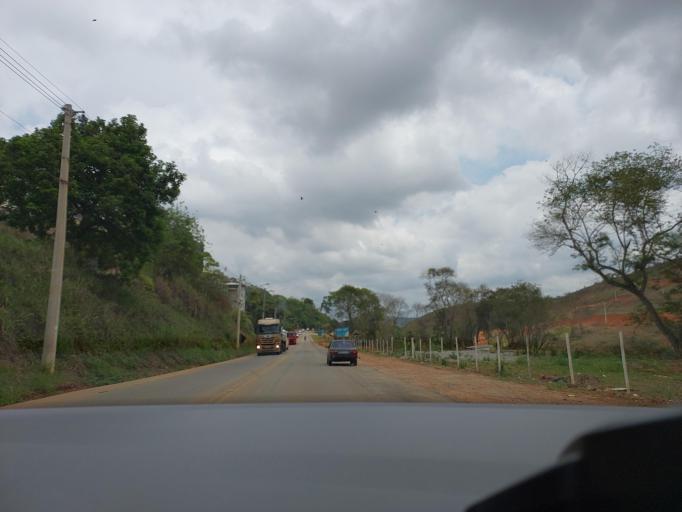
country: BR
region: Minas Gerais
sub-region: Ponte Nova
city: Ponte Nova
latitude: -20.3981
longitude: -42.8795
